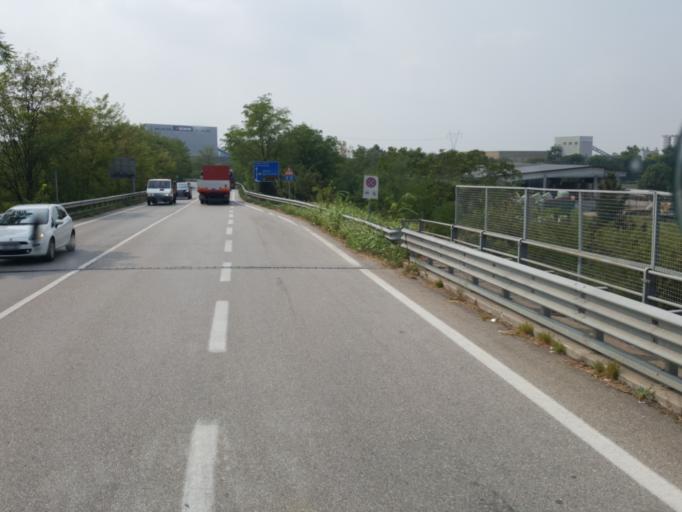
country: IT
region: Lombardy
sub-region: Provincia di Brescia
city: Novagli
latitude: 45.3836
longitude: 10.4505
